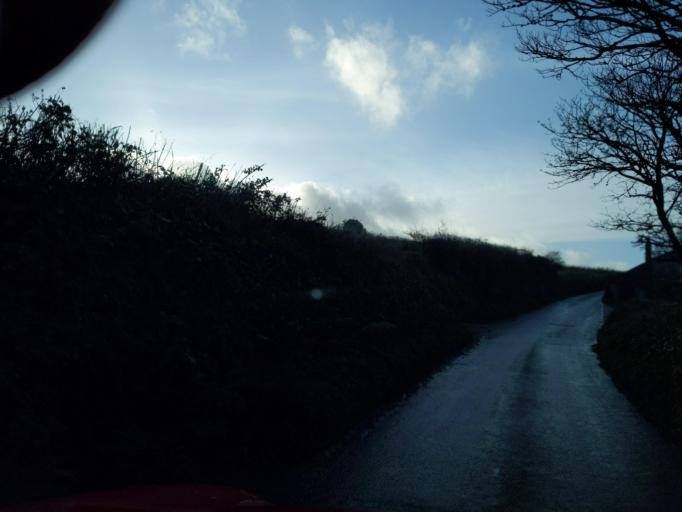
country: GB
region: England
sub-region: Cornwall
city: Fowey
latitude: 50.3332
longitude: -4.5973
